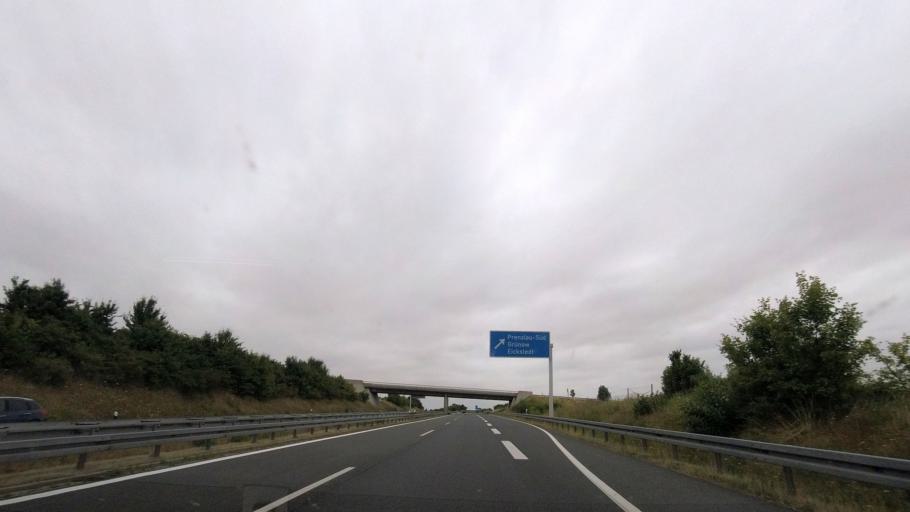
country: DE
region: Brandenburg
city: Grunow
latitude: 53.3053
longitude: 13.9902
